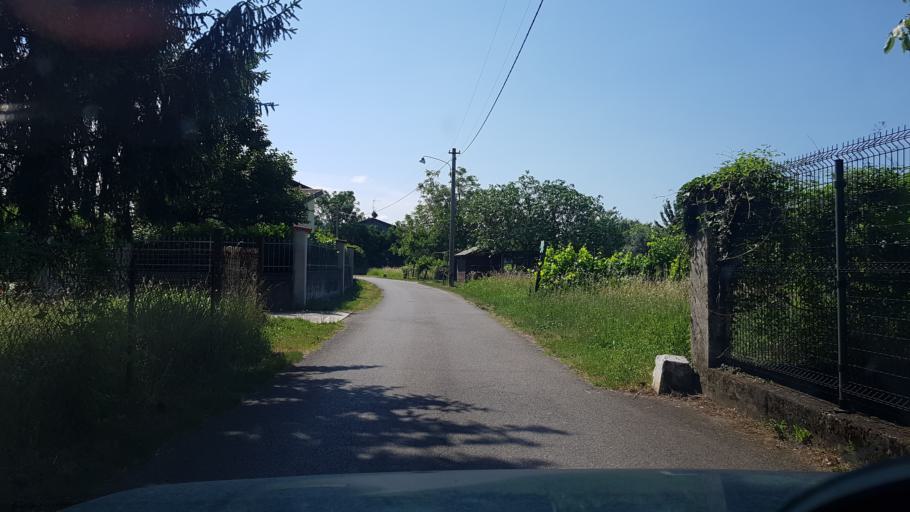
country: SI
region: Nova Gorica
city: Nova Gorica
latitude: 45.9623
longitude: 13.6300
